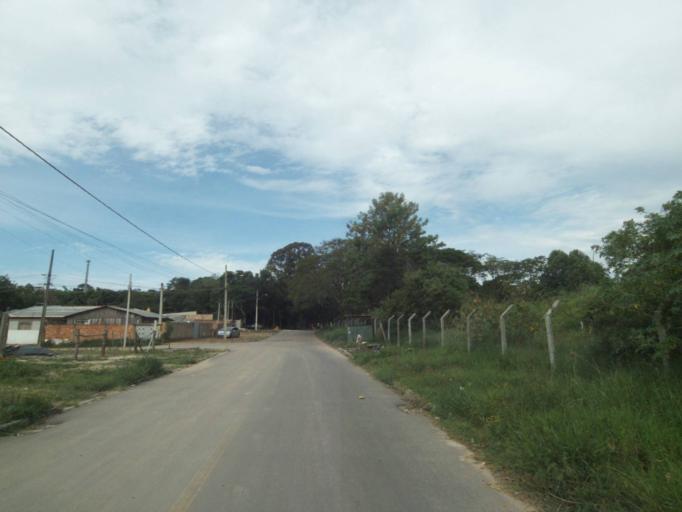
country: BR
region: Parana
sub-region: Pinhais
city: Pinhais
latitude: -25.4223
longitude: -49.2116
